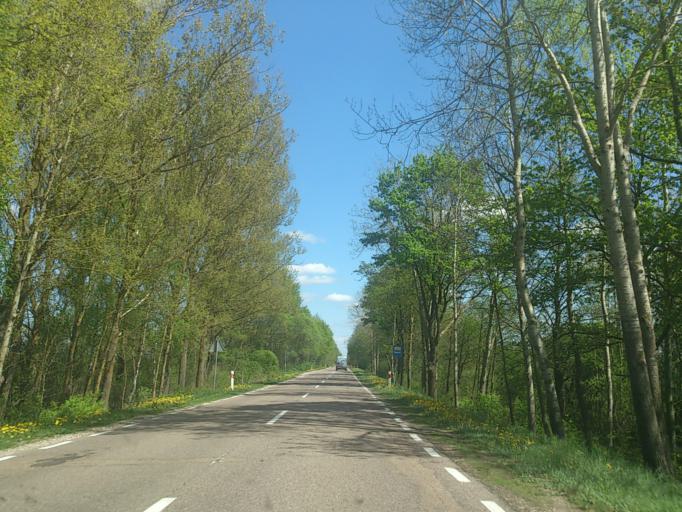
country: PL
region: Podlasie
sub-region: Powiat lomzynski
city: Wizna
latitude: 53.2023
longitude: 22.4420
